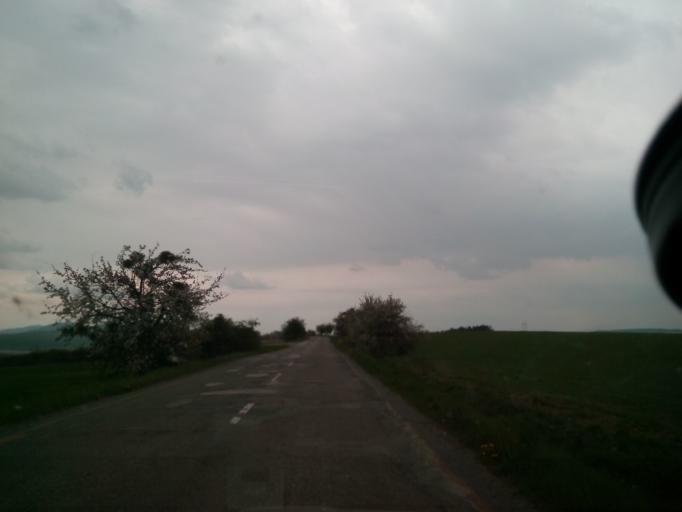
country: SK
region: Kosicky
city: Secovce
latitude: 48.7670
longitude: 21.4691
